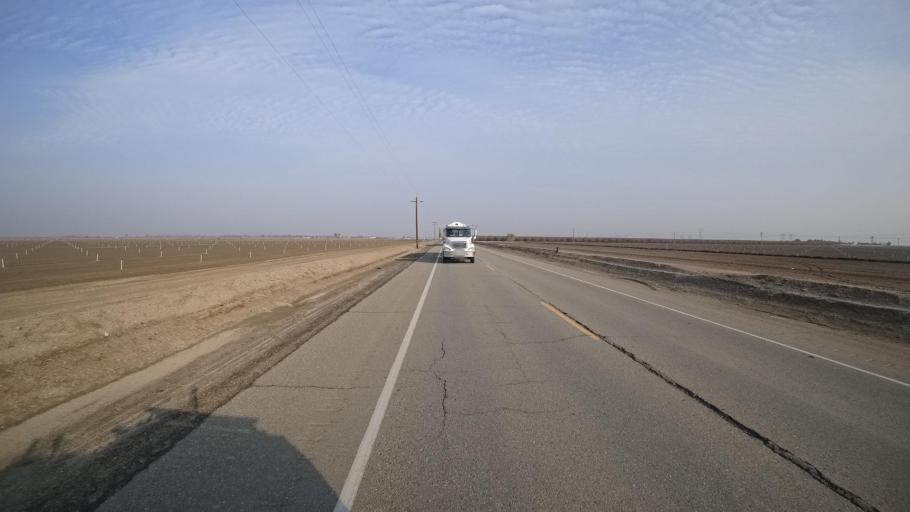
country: US
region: California
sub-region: Kern County
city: Weedpatch
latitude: 35.1560
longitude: -118.9147
